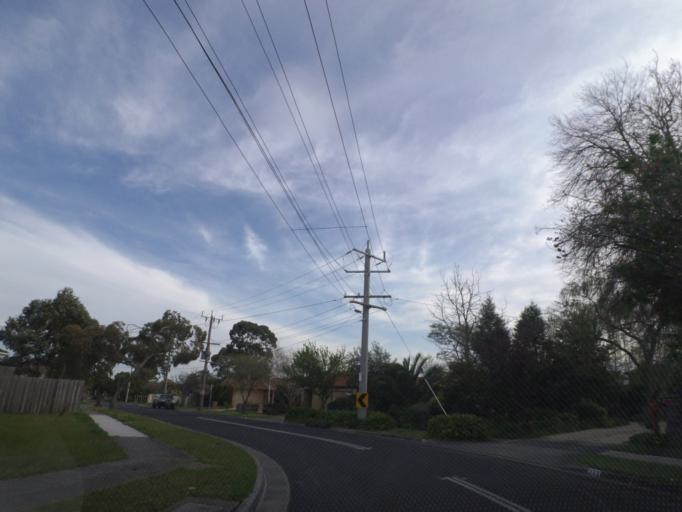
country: AU
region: Victoria
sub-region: Knox
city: Knoxfield
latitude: -37.8873
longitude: 145.2406
